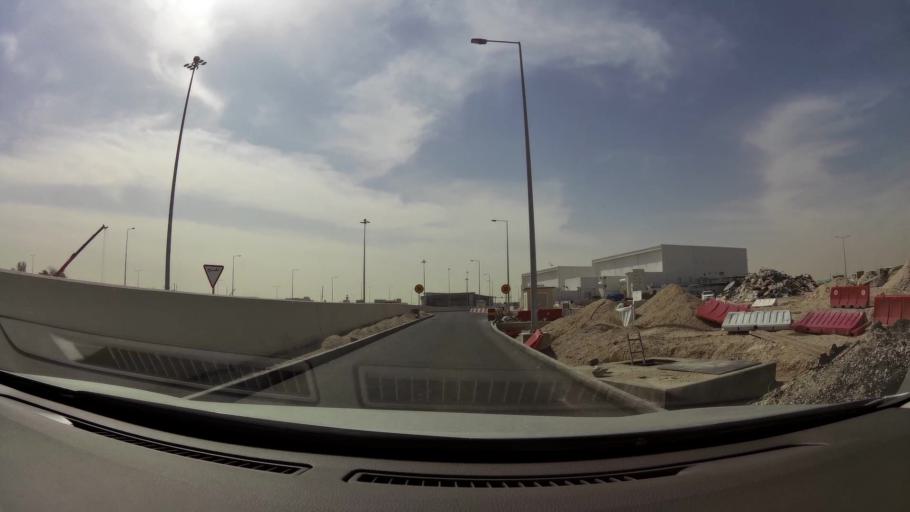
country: QA
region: Baladiyat ar Rayyan
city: Ar Rayyan
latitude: 25.3014
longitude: 51.4248
